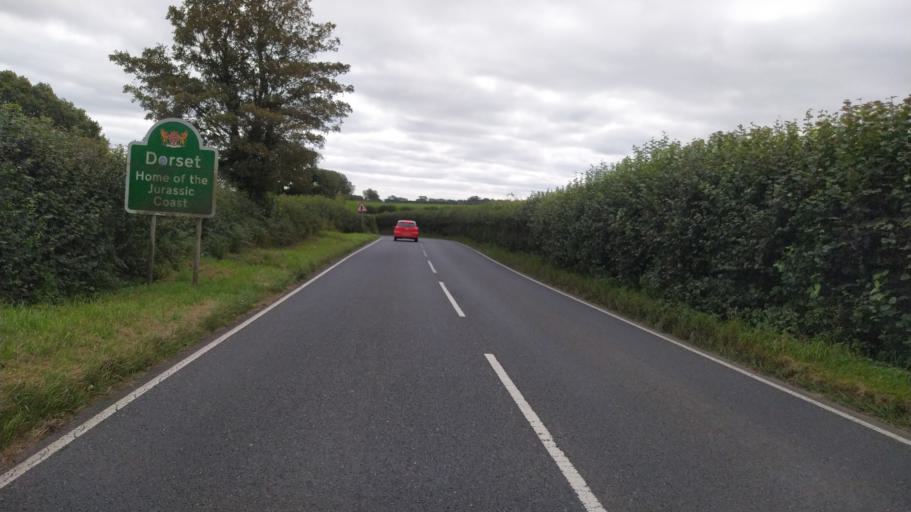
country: GB
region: England
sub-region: Somerset
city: Wincanton
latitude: 51.0610
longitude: -2.3490
